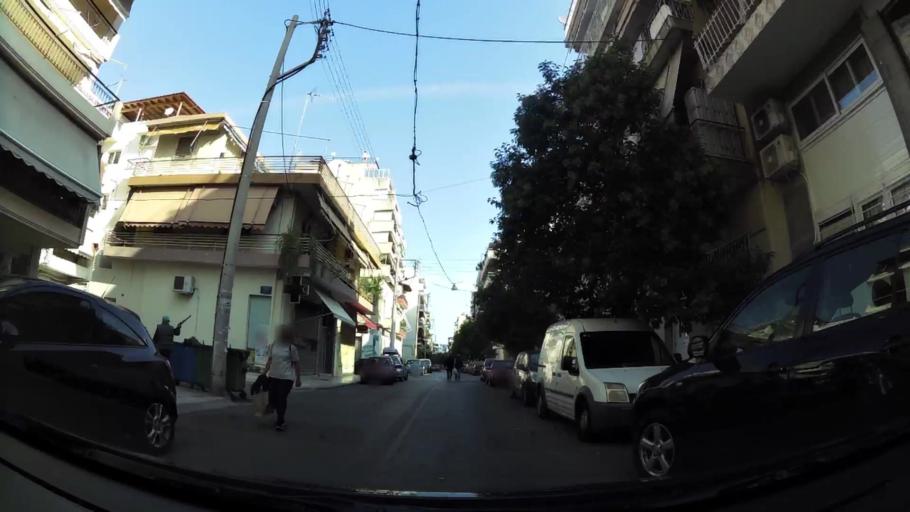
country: GR
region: Attica
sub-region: Nomarchia Athinas
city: Tavros
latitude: 37.9690
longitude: 23.7052
